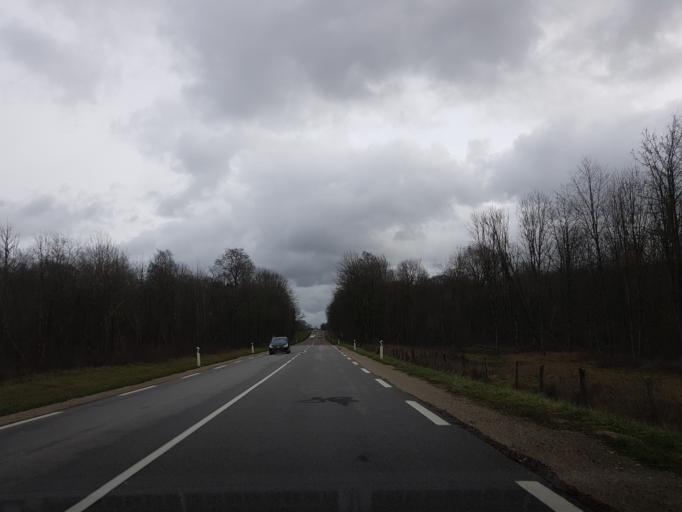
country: FR
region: Champagne-Ardenne
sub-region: Departement de la Haute-Marne
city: Fayl-Billot
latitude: 47.7961
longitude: 5.5655
